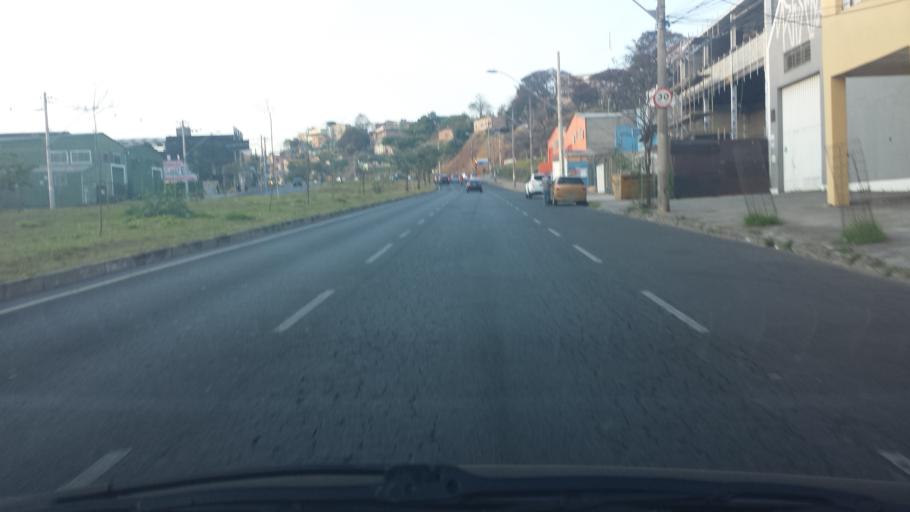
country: BR
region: Minas Gerais
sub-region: Belo Horizonte
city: Belo Horizonte
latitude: -19.8919
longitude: -43.9934
